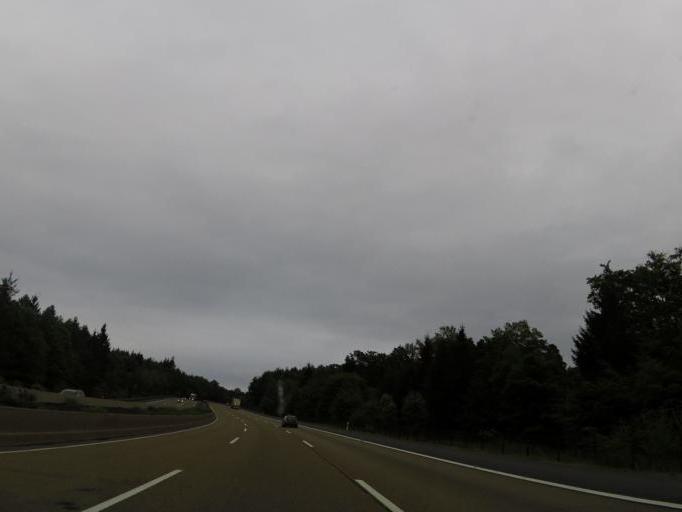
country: DE
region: Hesse
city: Schwarzenborn
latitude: 50.9489
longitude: 9.5131
